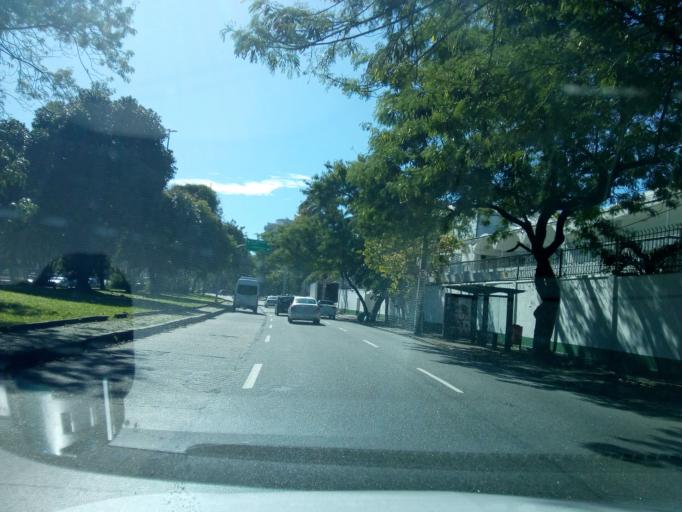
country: BR
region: Rio de Janeiro
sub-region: Rio De Janeiro
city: Rio de Janeiro
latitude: -22.9800
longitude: -43.2162
